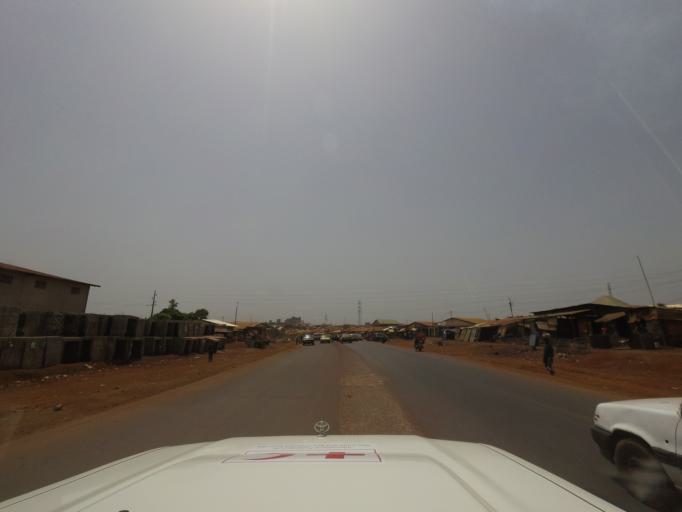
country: GN
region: Kindia
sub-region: Prefecture de Dubreka
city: Dubreka
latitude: 9.7218
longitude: -13.4756
